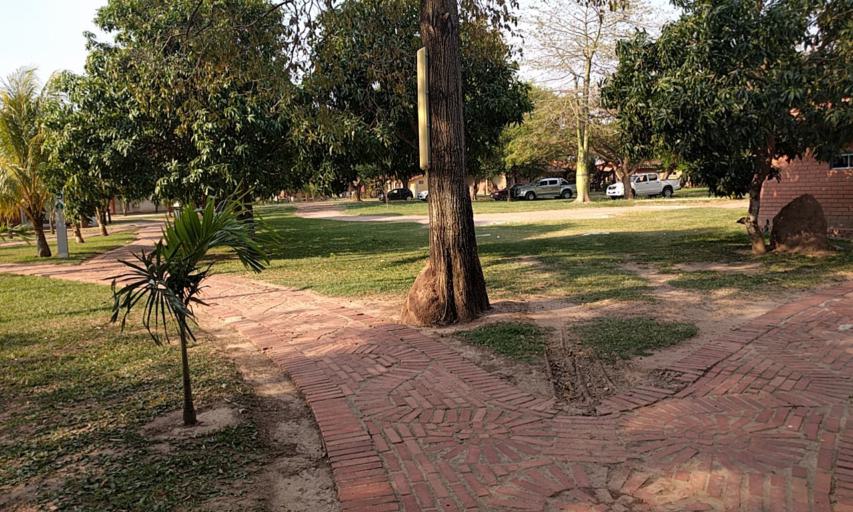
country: BO
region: Santa Cruz
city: Warnes
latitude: -17.4477
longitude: -63.1845
